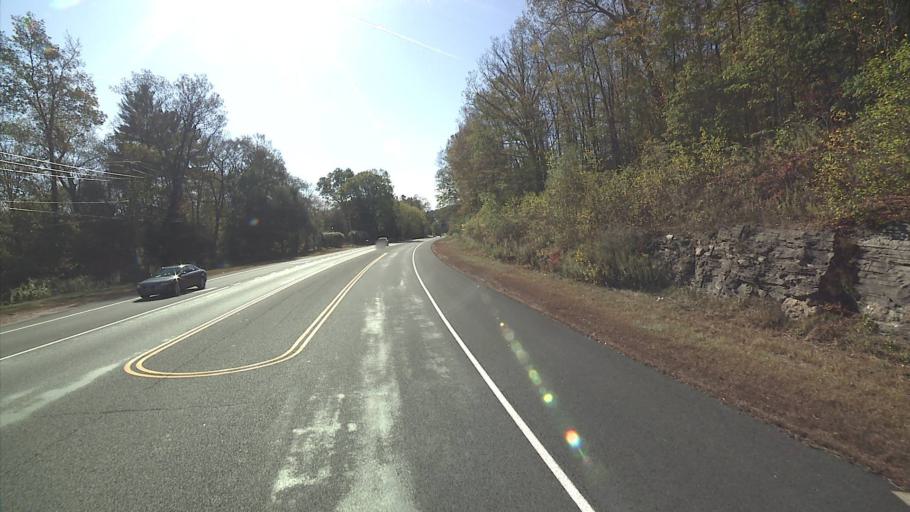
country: US
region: Connecticut
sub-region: Tolland County
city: Coventry Lake
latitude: 41.7679
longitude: -72.4065
